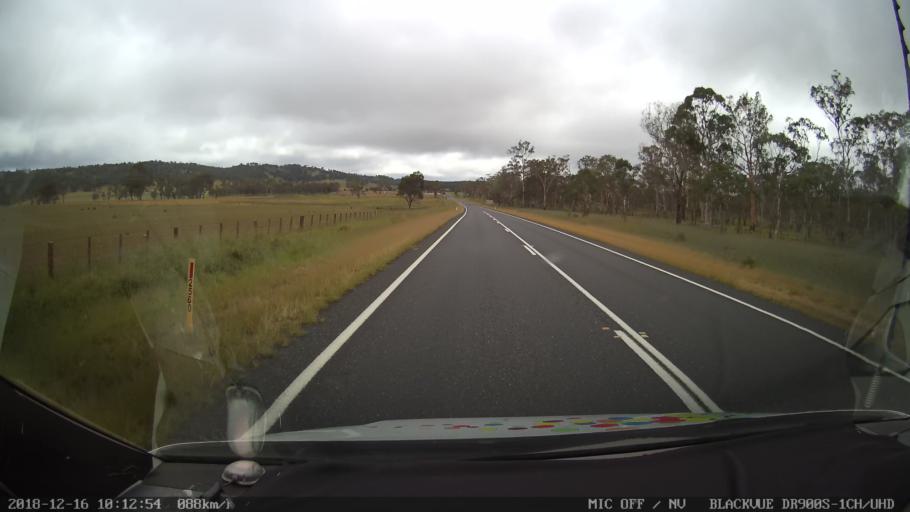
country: AU
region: New South Wales
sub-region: Glen Innes Severn
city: Glen Innes
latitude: -29.3022
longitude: 151.9462
